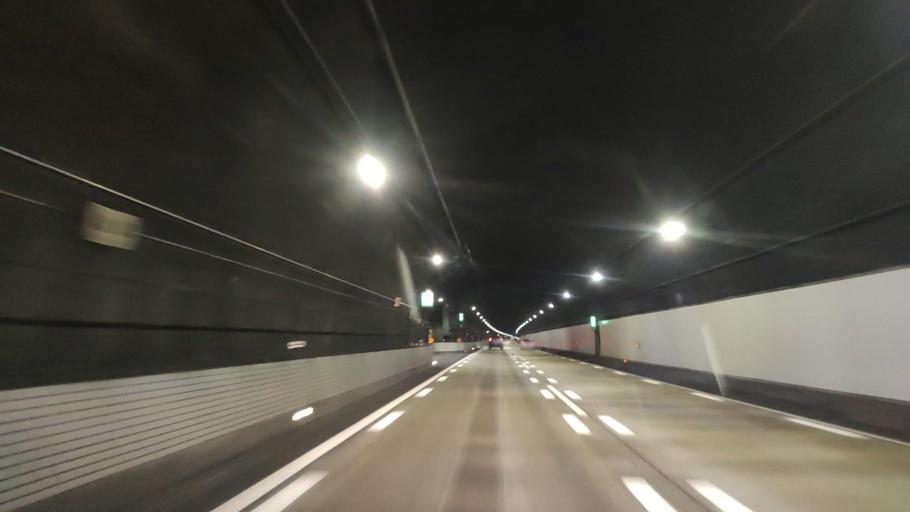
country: JP
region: Hiroshima
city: Fukuyama
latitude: 34.5012
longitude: 133.3235
